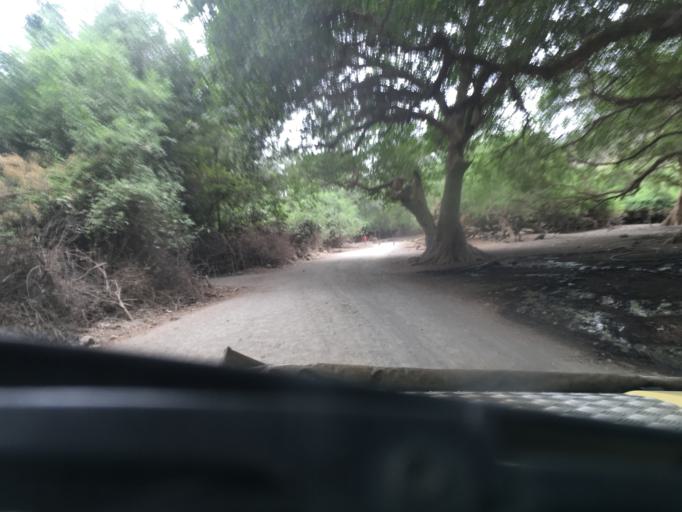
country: TZ
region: Arusha
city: Mto wa Mbu
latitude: -2.6190
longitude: 35.8795
